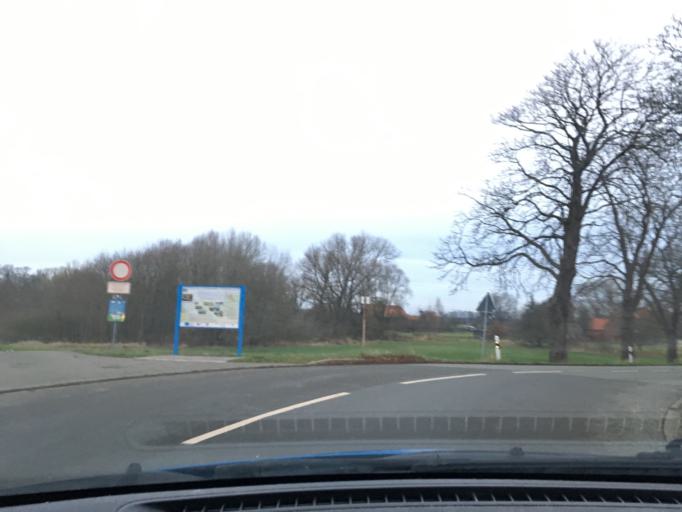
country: DE
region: Lower Saxony
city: Neu Darchau
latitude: 53.2376
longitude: 10.8935
